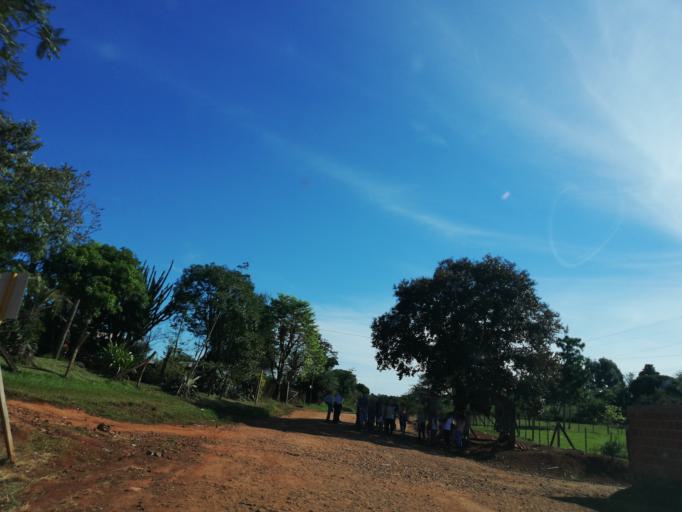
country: AR
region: Misiones
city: Dos de Mayo
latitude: -27.0142
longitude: -54.4495
